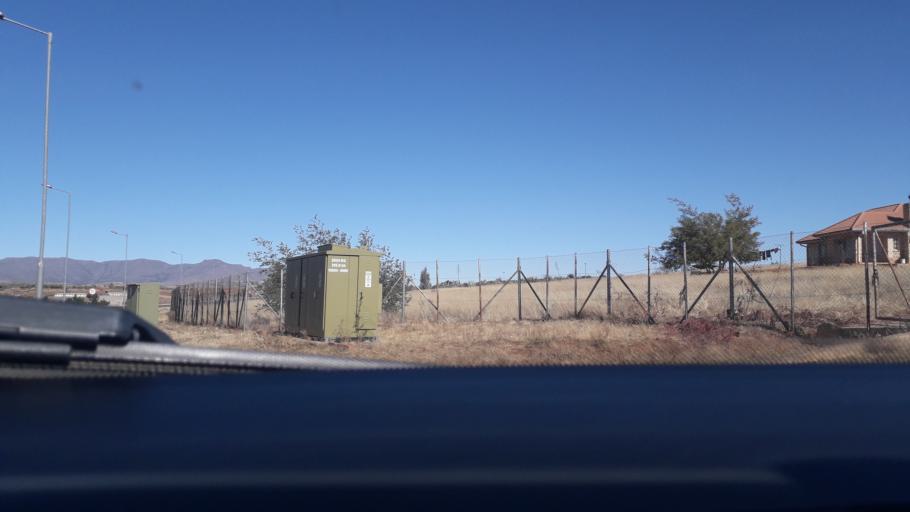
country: LS
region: Berea
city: Teyateyaneng
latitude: -29.3288
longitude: 27.7731
